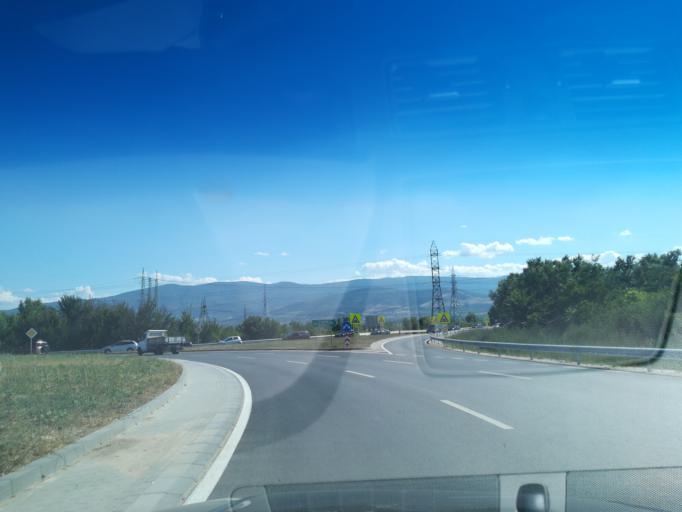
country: BG
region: Plovdiv
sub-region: Obshtina Plovdiv
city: Plovdiv
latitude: 42.0993
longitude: 24.7876
